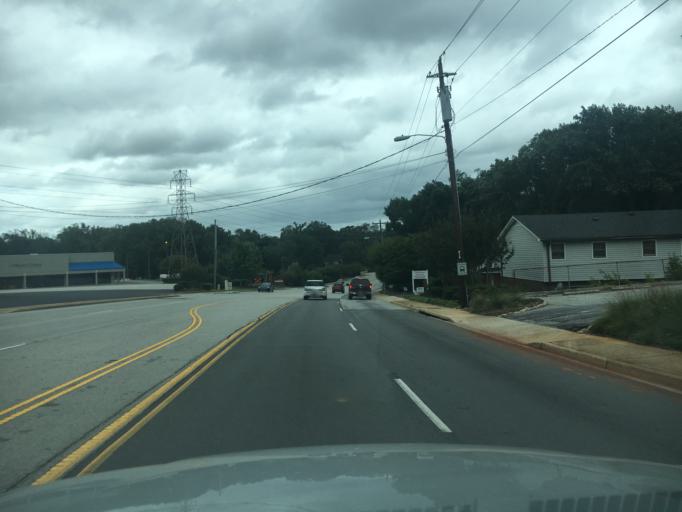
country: US
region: South Carolina
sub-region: Greenville County
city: Greenville
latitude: 34.8846
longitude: -82.3766
